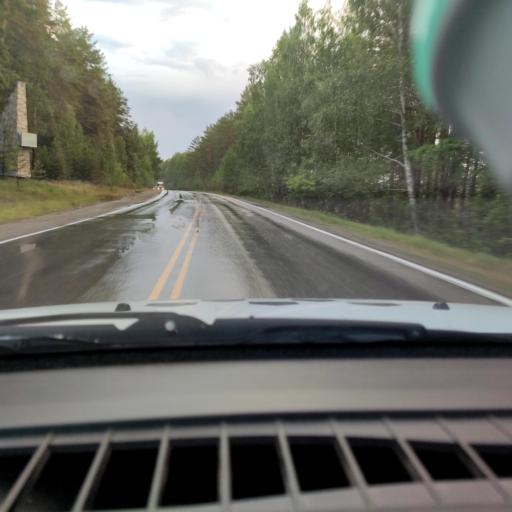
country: RU
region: Chelyabinsk
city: Kyshtym
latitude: 55.7357
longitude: 60.5380
